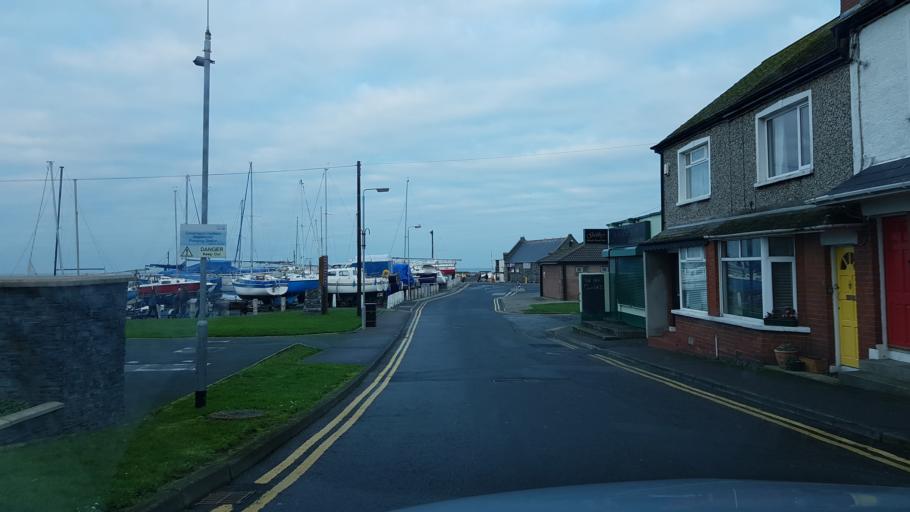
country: GB
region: Northern Ireland
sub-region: North Down District
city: Bangor
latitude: 54.6760
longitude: -5.6174
